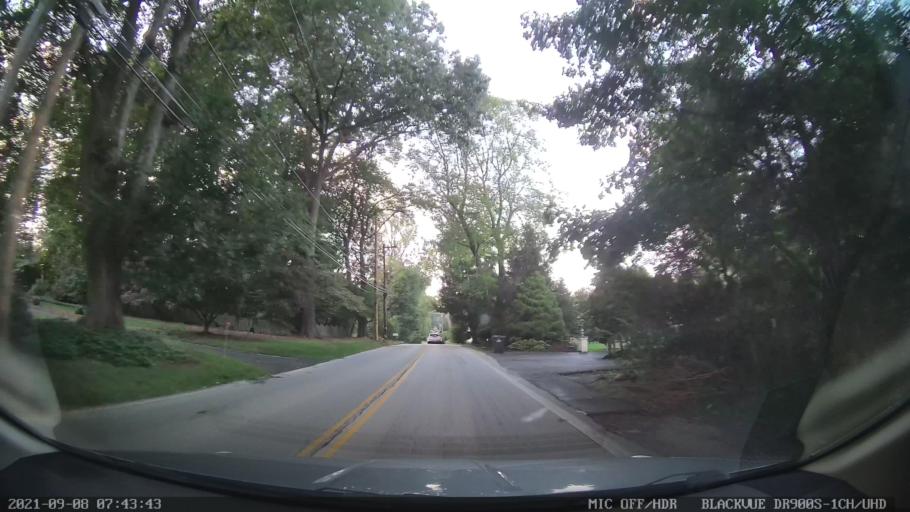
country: US
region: Pennsylvania
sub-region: Delaware County
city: Wayne
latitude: 40.0668
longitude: -75.3765
